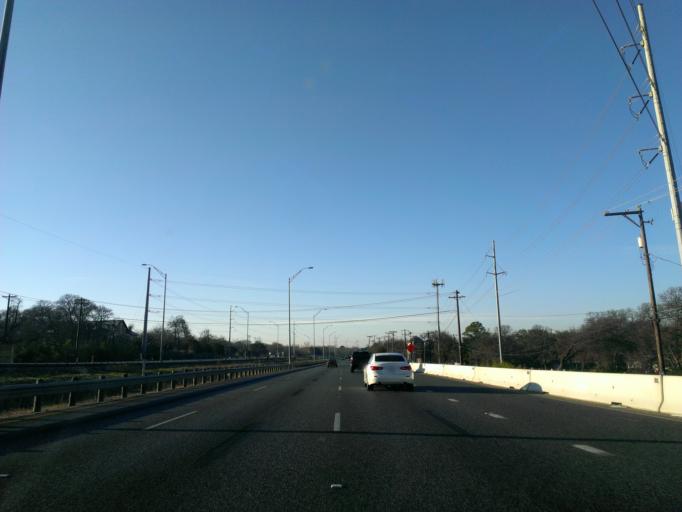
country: US
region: Texas
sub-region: Travis County
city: Austin
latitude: 30.2967
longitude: -97.7589
